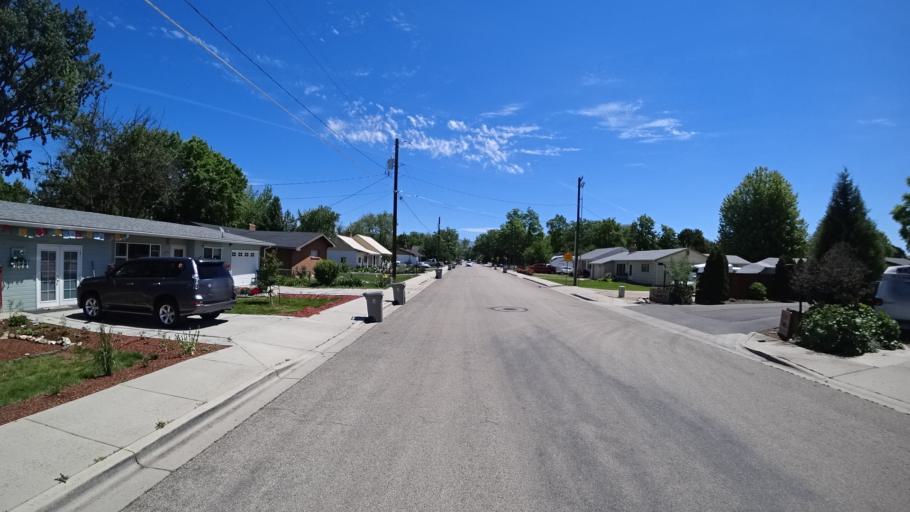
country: US
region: Idaho
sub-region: Ada County
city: Garden City
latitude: 43.5988
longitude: -116.2407
